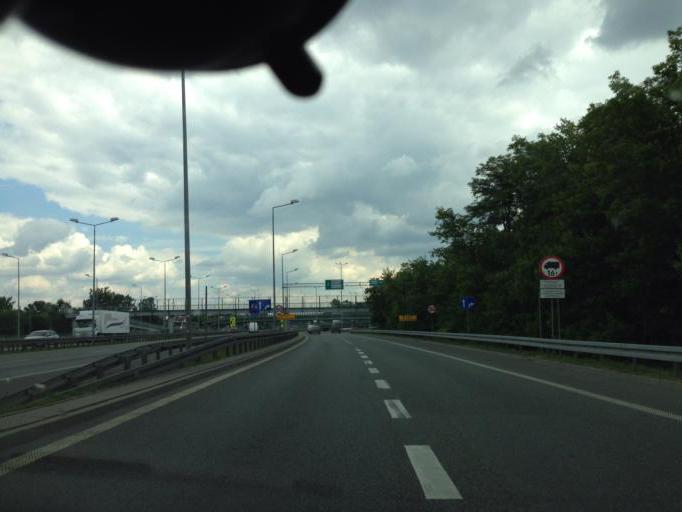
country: PL
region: Masovian Voivodeship
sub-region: Warszawa
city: Bemowo
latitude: 52.2543
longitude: 20.9460
